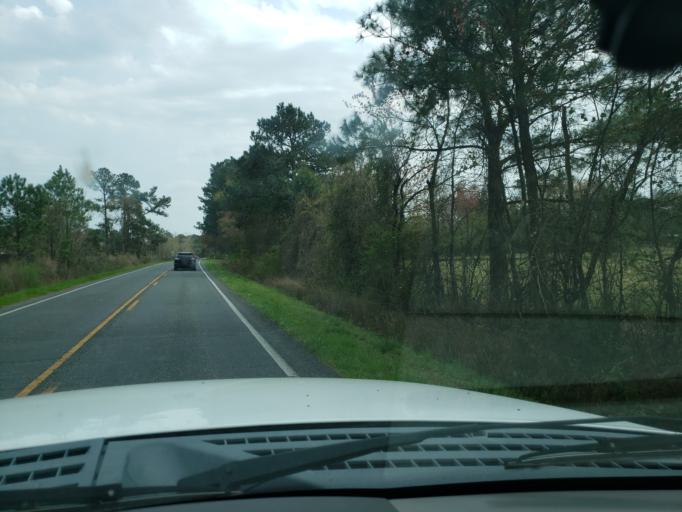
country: US
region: North Carolina
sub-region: Duplin County
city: Beulaville
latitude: 34.7729
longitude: -77.8086
